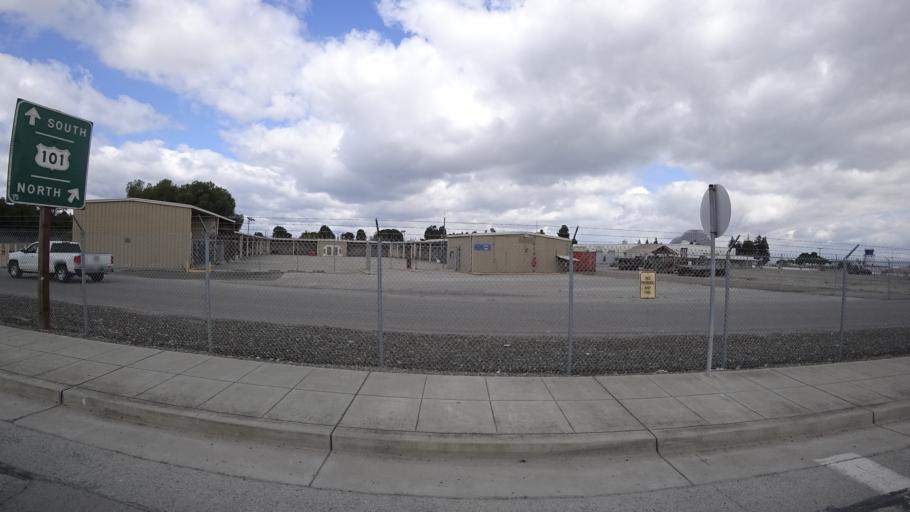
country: US
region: California
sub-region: Santa Clara County
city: Mountain View
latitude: 37.4052
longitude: -122.0511
